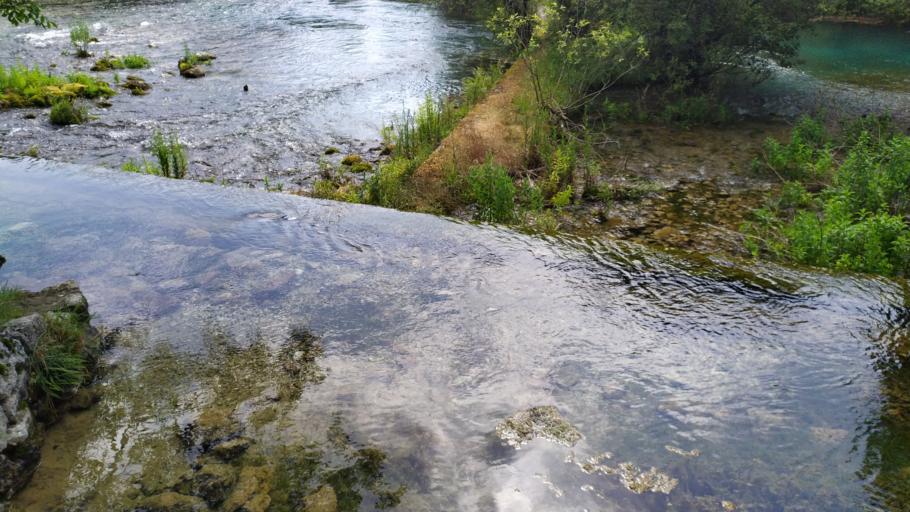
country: IT
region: Friuli Venezia Giulia
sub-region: Provincia di Pordenone
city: Polcenigo
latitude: 46.0215
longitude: 12.4750
